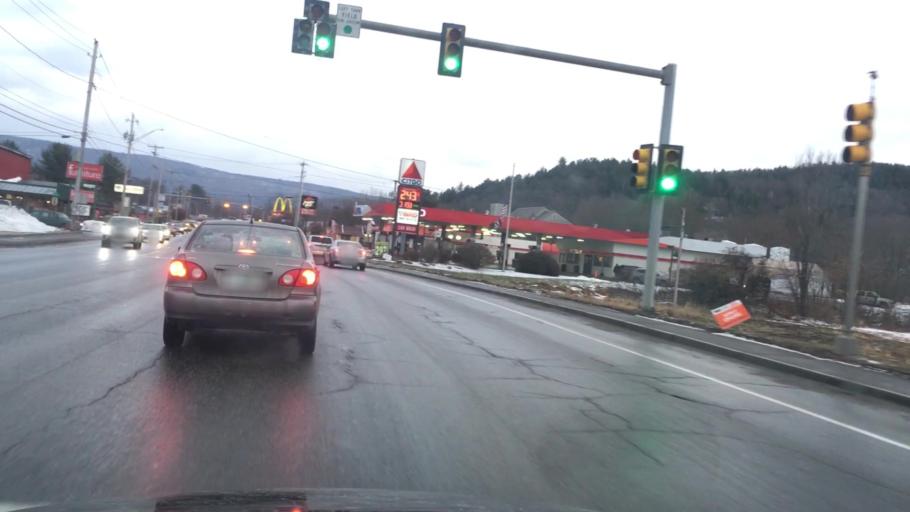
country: US
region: New Hampshire
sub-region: Sullivan County
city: Claremont
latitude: 43.3708
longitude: -72.3269
